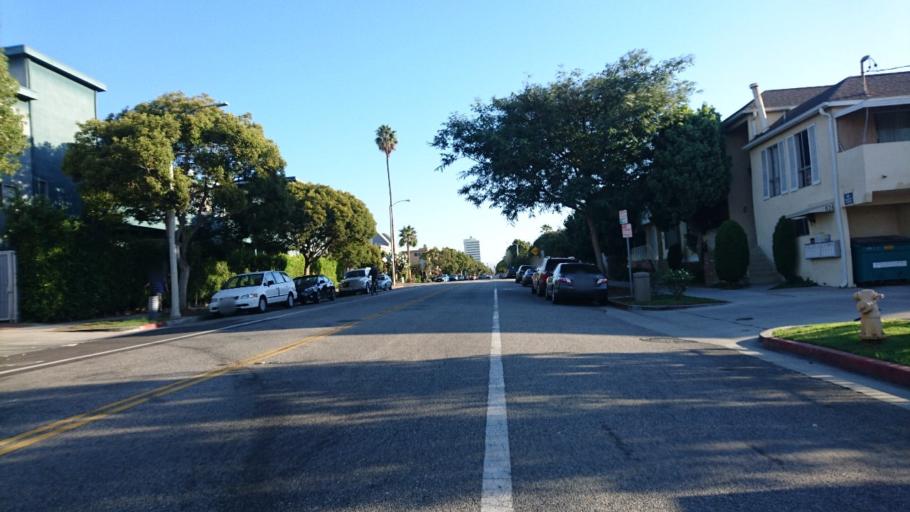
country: US
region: California
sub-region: Los Angeles County
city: Santa Monica
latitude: 34.0211
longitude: -118.4926
